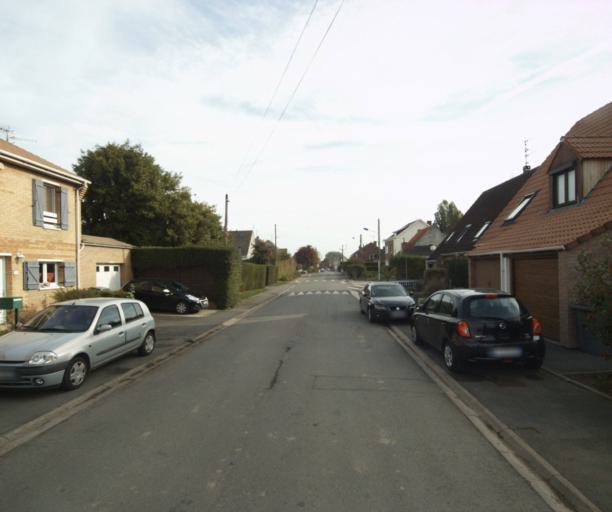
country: FR
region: Nord-Pas-de-Calais
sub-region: Departement du Nord
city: Sainghin-en-Weppes
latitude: 50.5569
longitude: 2.8998
